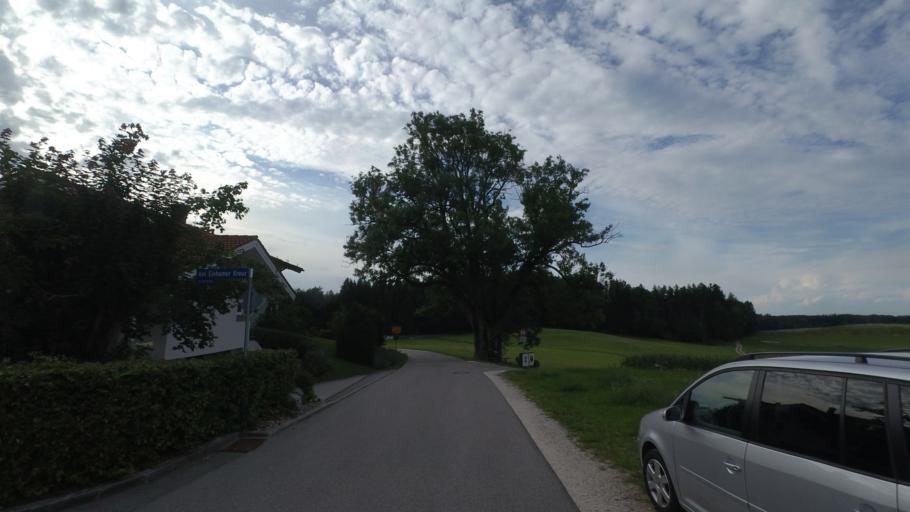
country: DE
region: Bavaria
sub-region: Upper Bavaria
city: Vachendorf
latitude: 47.8637
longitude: 12.6078
